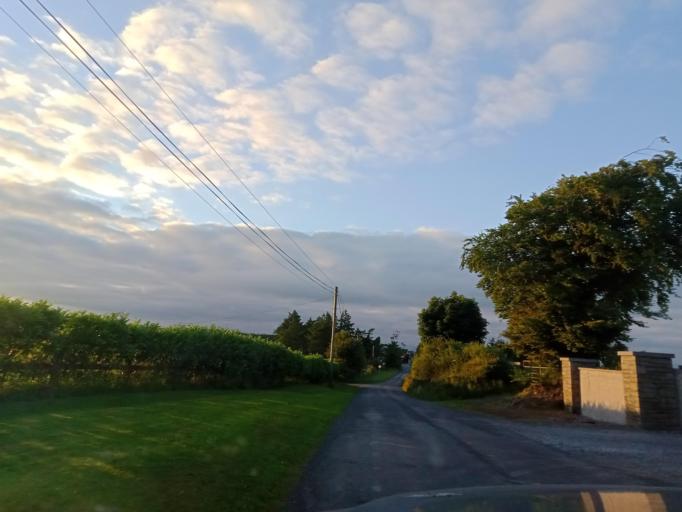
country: IE
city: Ballylinan
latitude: 52.9008
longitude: -7.1318
